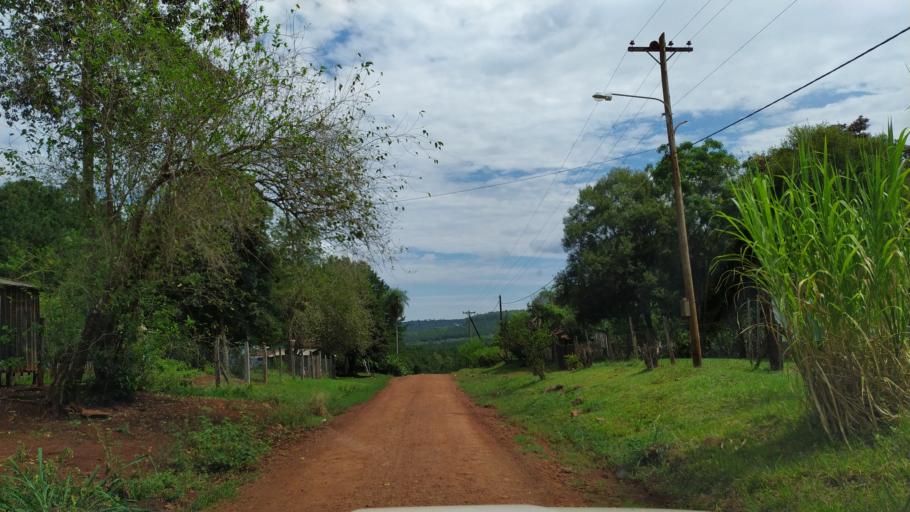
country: AR
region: Misiones
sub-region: Departamento de Eldorado
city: Eldorado
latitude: -26.5302
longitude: -54.6019
